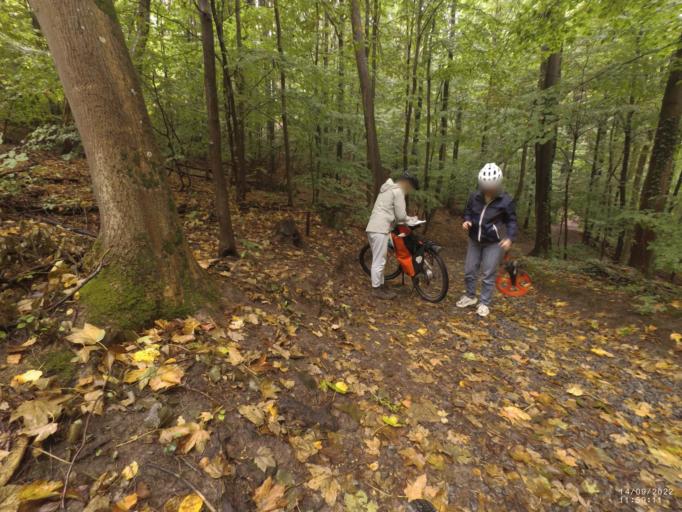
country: DE
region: Bavaria
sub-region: Regierungsbezirk Unterfranken
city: Johannesberg
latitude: 50.0154
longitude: 9.1340
